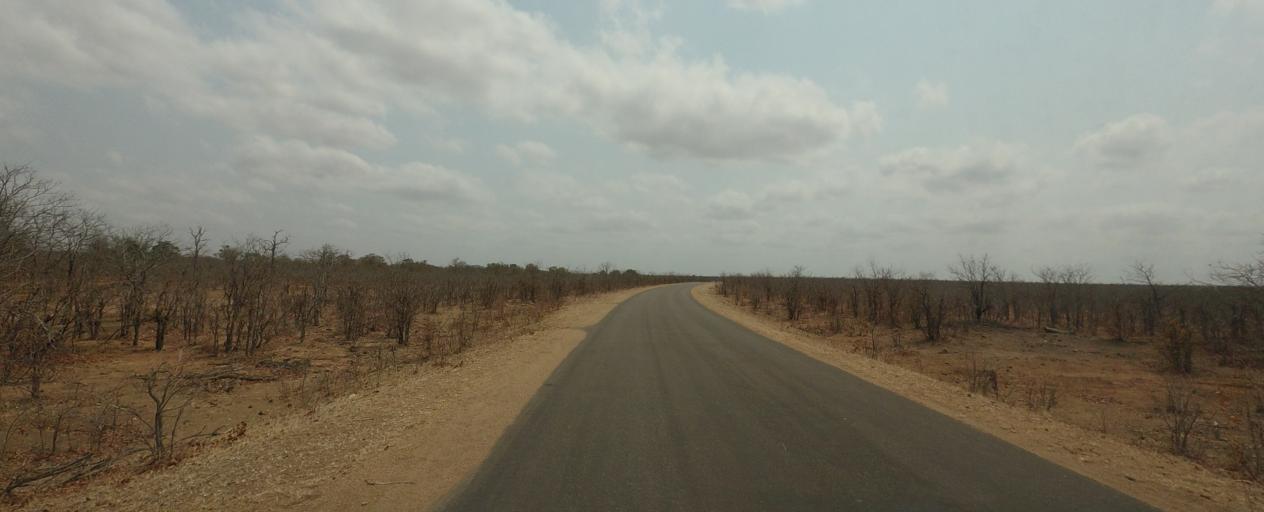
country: ZA
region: Limpopo
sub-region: Mopani District Municipality
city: Phalaborwa
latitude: -23.5480
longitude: 31.4288
